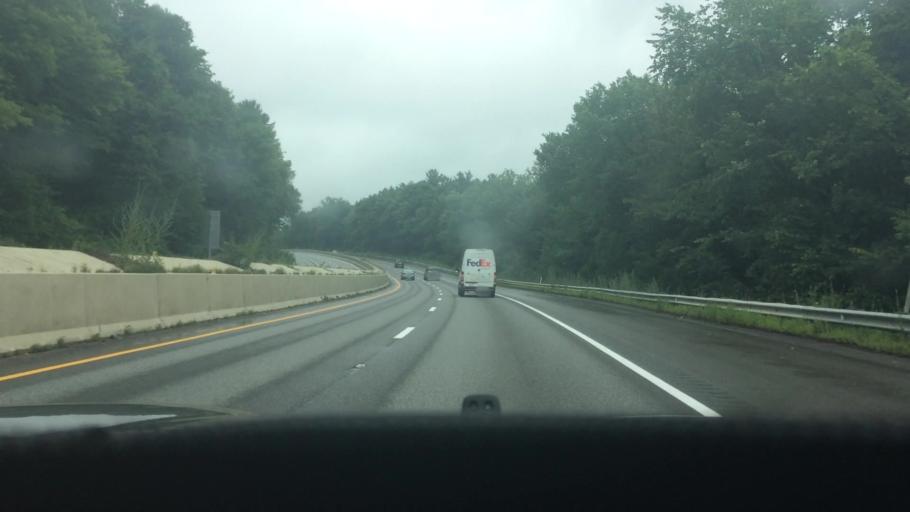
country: US
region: Massachusetts
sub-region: Worcester County
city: Leominster
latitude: 42.5506
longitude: -71.7661
